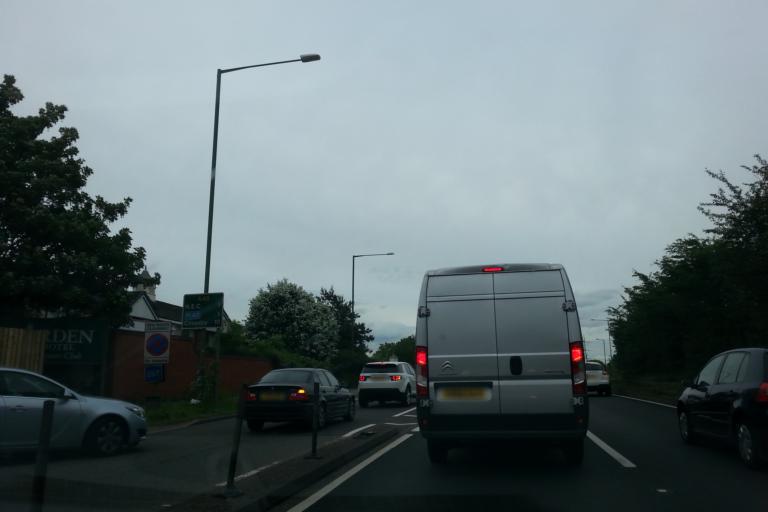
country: GB
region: England
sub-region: Solihull
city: Bickenhill
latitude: 52.4446
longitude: -1.7218
